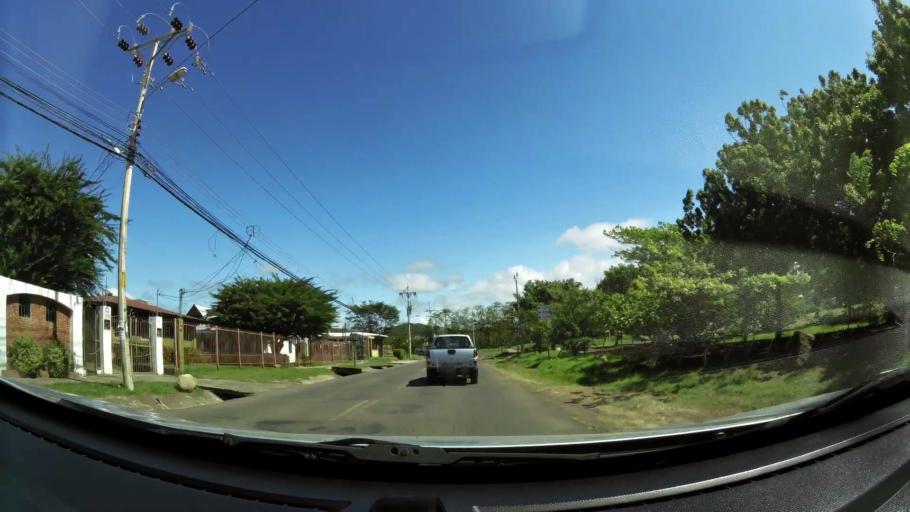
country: CR
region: Guanacaste
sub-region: Canton de Canas
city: Canas
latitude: 10.4317
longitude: -85.0867
